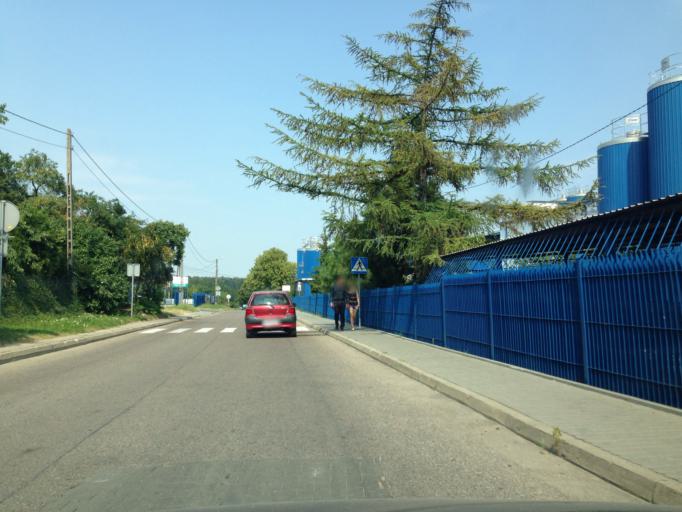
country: PL
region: Kujawsko-Pomorskie
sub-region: Powiat rypinski
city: Rypin
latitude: 53.0737
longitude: 19.4017
